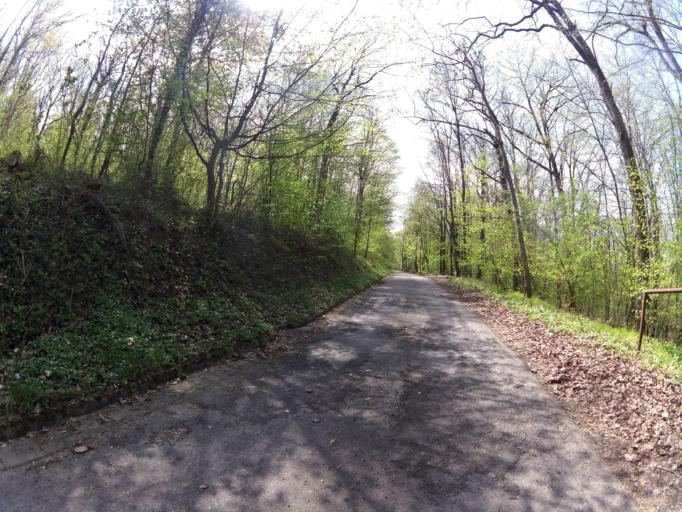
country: DE
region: Bavaria
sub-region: Regierungsbezirk Unterfranken
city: Winterhausen
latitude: 49.6988
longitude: 10.0041
